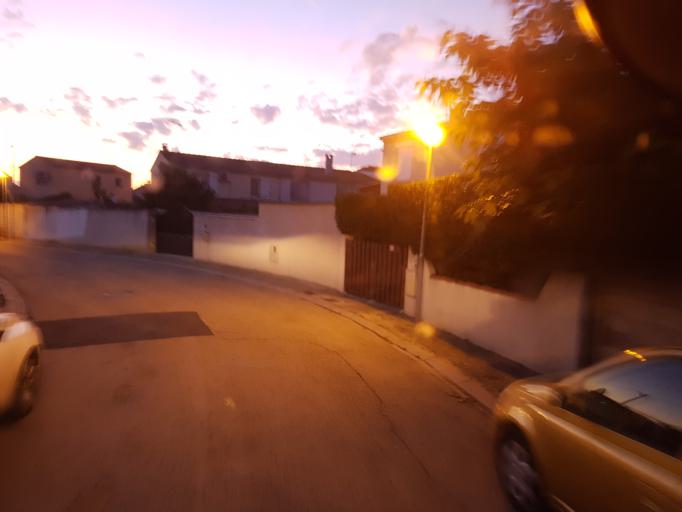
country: FR
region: Languedoc-Roussillon
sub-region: Departement du Gard
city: Bellegarde
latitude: 43.7488
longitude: 4.5180
